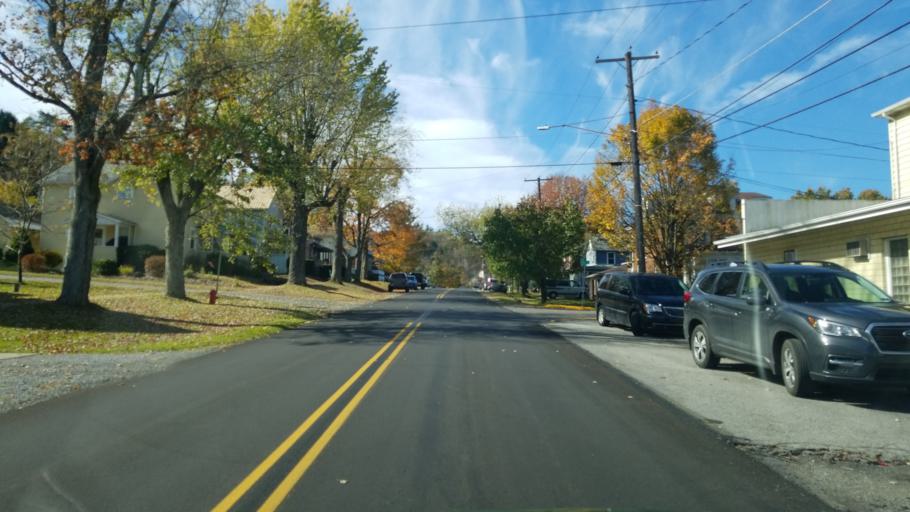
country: US
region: Pennsylvania
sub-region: Jefferson County
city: Brockway
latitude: 41.2475
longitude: -78.7983
